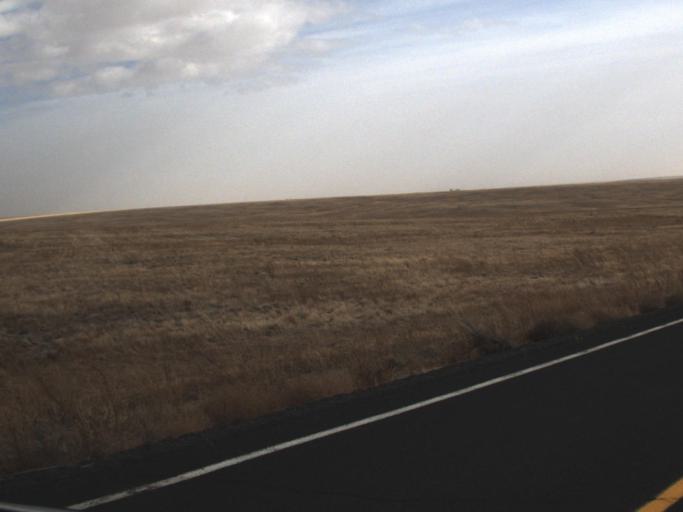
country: US
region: Washington
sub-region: Adams County
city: Ritzville
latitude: 47.4382
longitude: -118.7269
